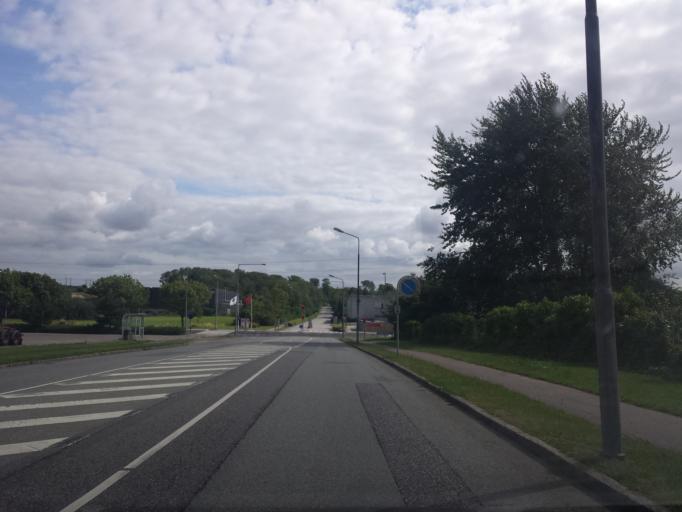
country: DK
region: South Denmark
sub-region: Sonderborg Kommune
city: Nordborg
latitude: 55.0334
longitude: 9.8091
